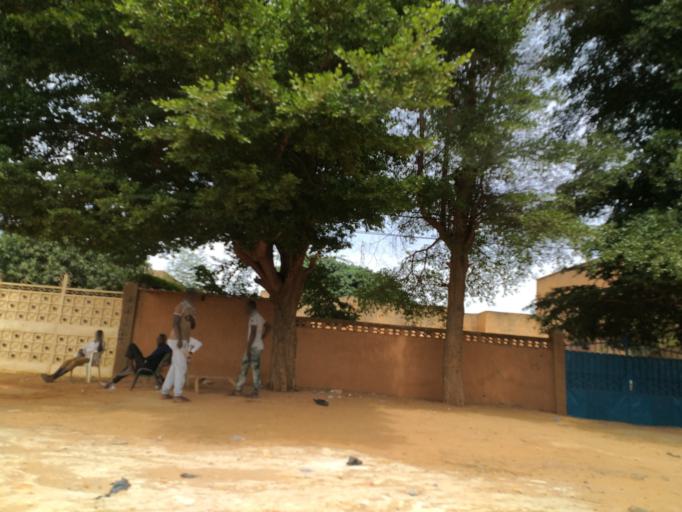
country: NE
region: Niamey
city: Niamey
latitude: 13.5405
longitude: 2.0659
